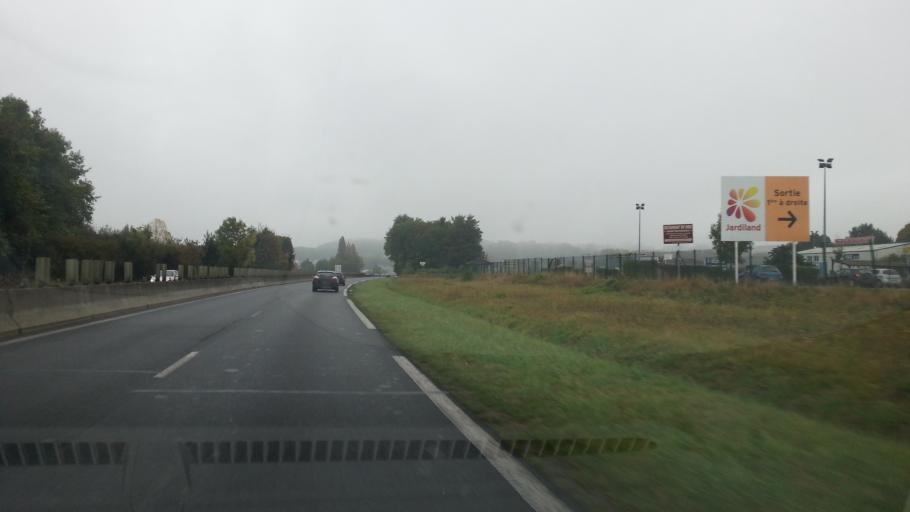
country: FR
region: Picardie
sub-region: Departement de l'Oise
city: Rantigny
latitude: 49.3411
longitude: 2.4336
